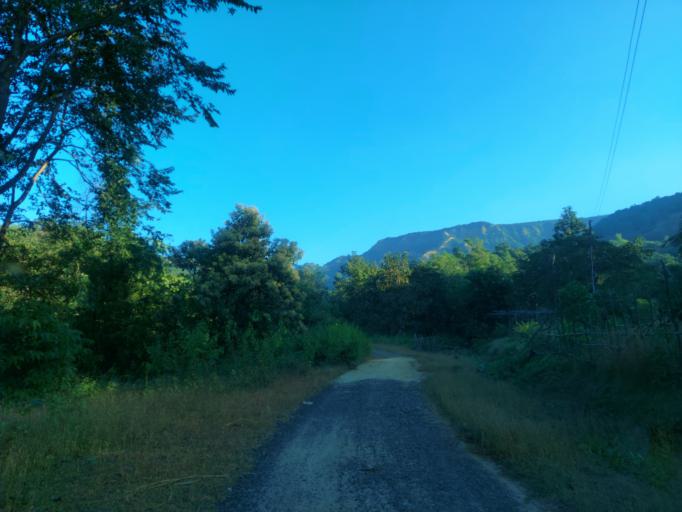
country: IN
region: Maharashtra
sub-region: Sindhudurg
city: Kudal
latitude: 16.0729
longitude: 73.8255
